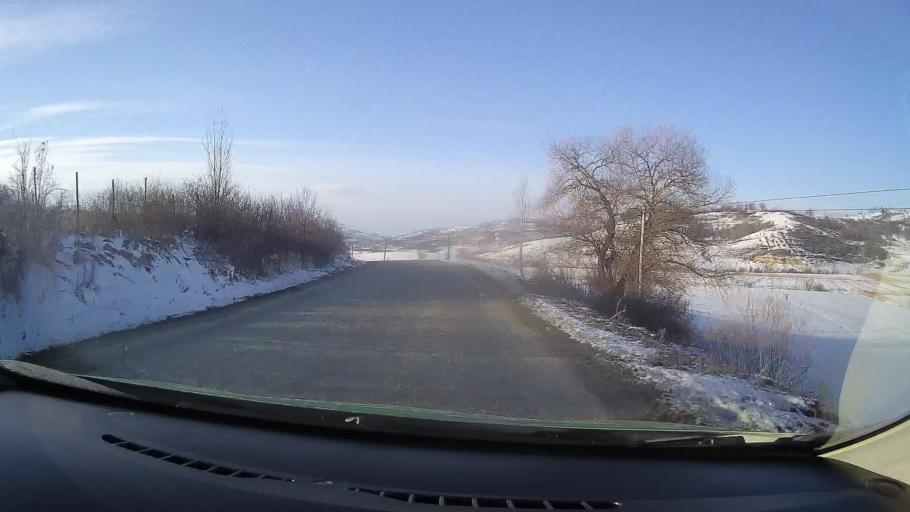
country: RO
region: Sibiu
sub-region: Comuna Merghindeal
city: Merghindeal
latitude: 45.9683
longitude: 24.7119
